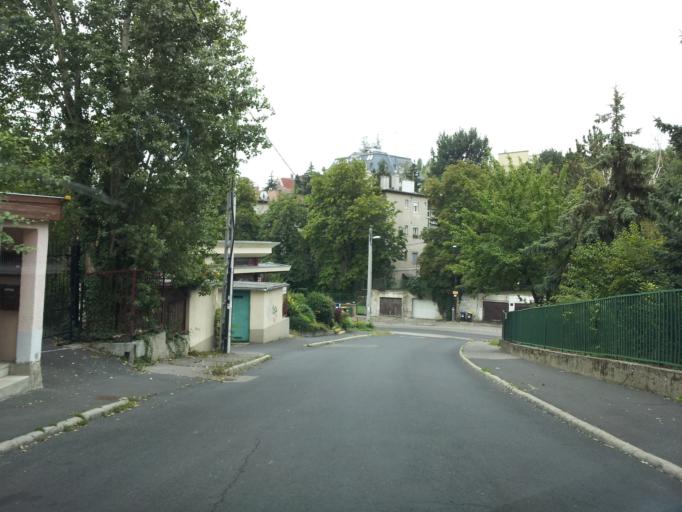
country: HU
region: Budapest
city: Budapest II. keruelet
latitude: 47.5194
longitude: 19.0132
